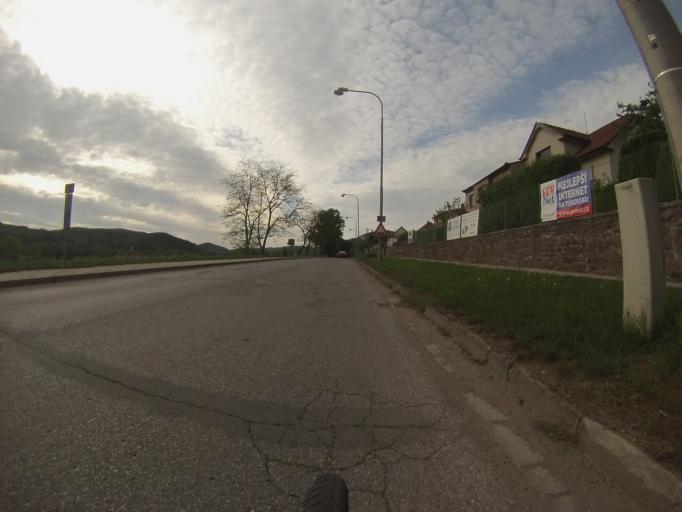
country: CZ
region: South Moravian
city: Tisnov
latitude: 49.3386
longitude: 16.4351
